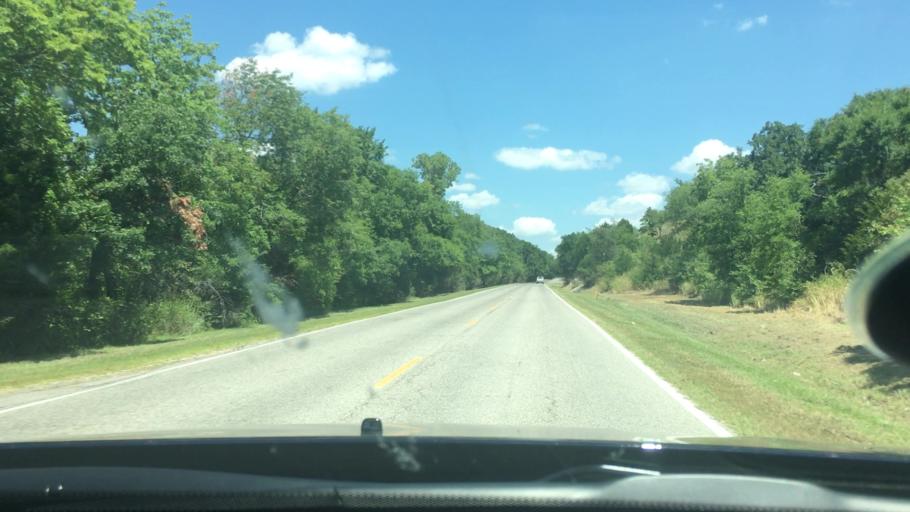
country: US
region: Oklahoma
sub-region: Carter County
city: Dickson
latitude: 34.3114
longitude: -96.9625
